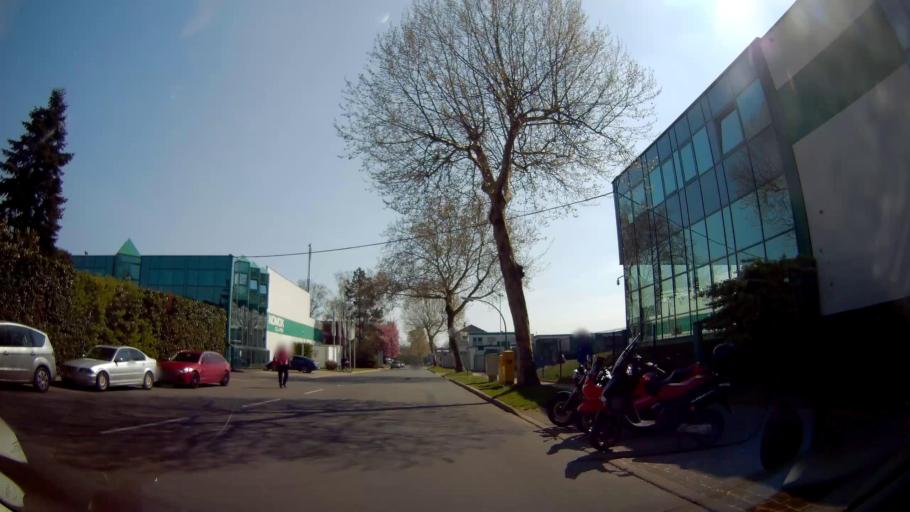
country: DE
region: North Rhine-Westphalia
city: Bochum-Hordel
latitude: 51.4851
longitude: 7.1576
